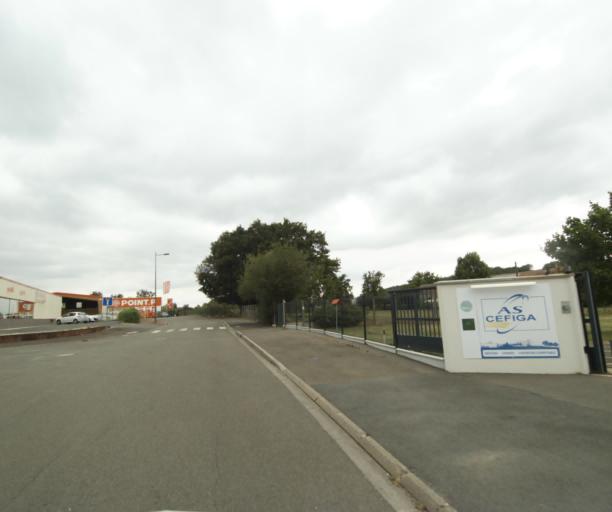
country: FR
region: Pays de la Loire
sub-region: Departement de la Sarthe
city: Solesmes
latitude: 47.8377
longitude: -0.3049
